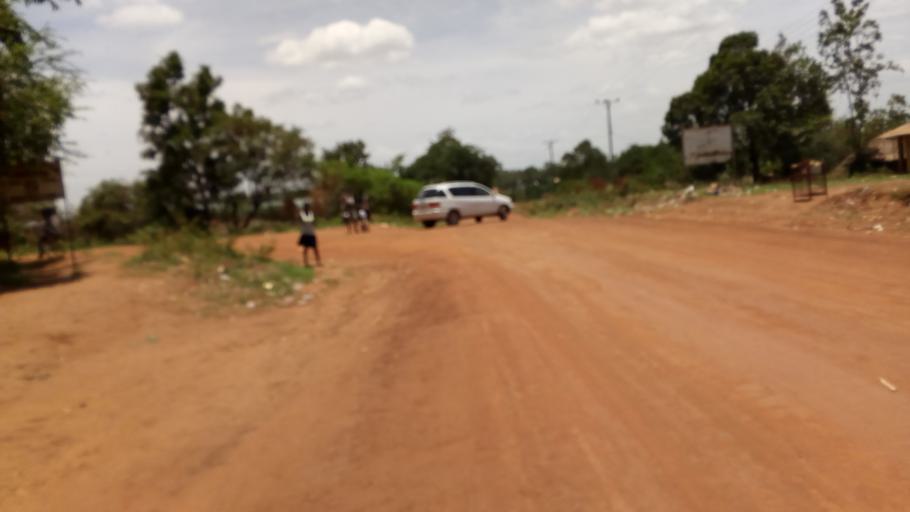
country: UG
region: Northern Region
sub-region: Gulu District
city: Gulu
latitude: 2.7976
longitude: 32.3140
